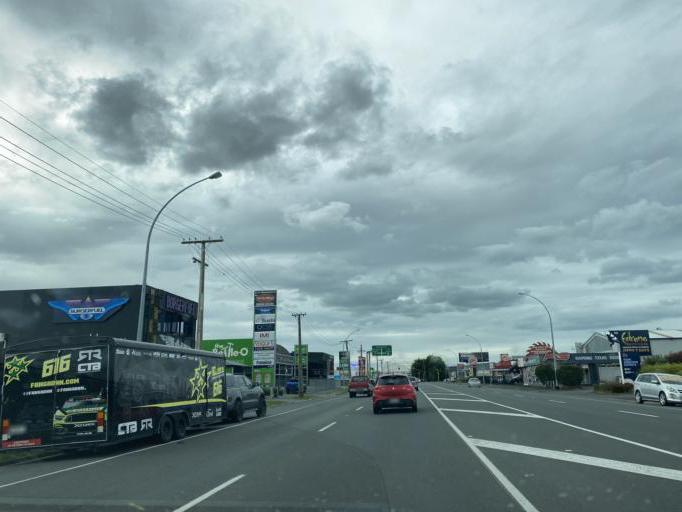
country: NZ
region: Waikato
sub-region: Hamilton City
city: Hamilton
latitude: -37.7915
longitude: 175.2601
